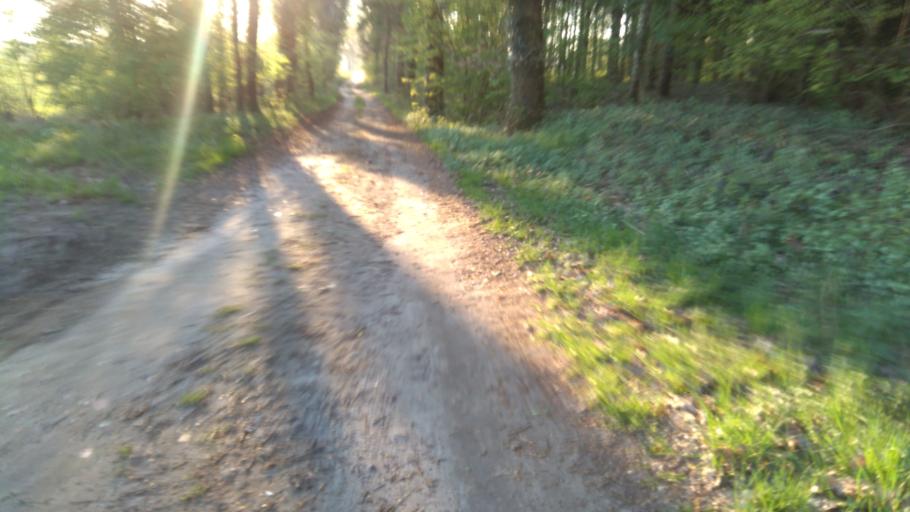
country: DE
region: Lower Saxony
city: Harsefeld
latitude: 53.4685
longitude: 9.4966
